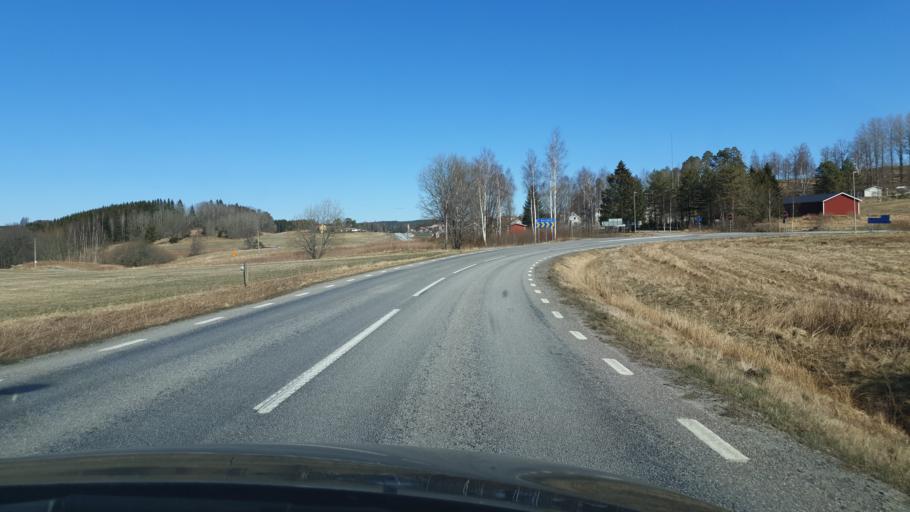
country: SE
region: Vaestra Goetaland
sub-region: Tanums Kommun
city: Tanumshede
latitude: 58.7685
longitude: 11.5552
